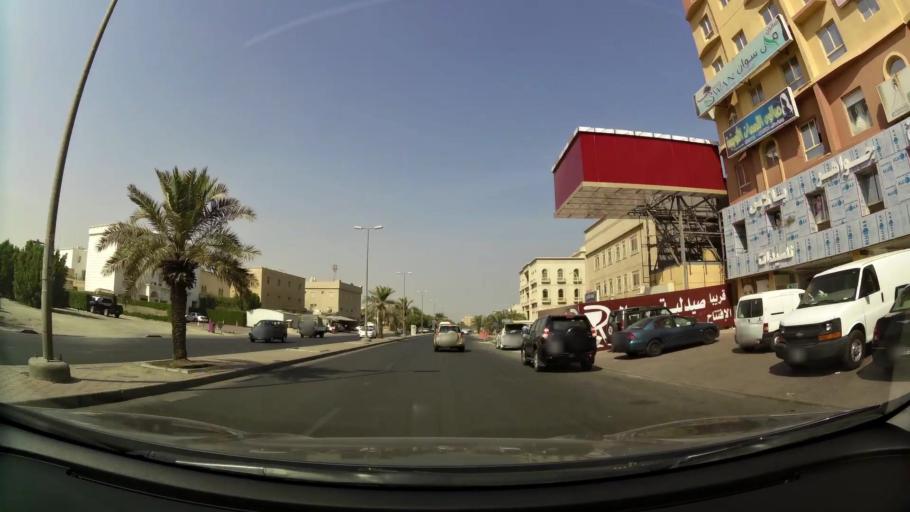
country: KW
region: Al Ahmadi
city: Al Fahahil
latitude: 29.0834
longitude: 48.1229
